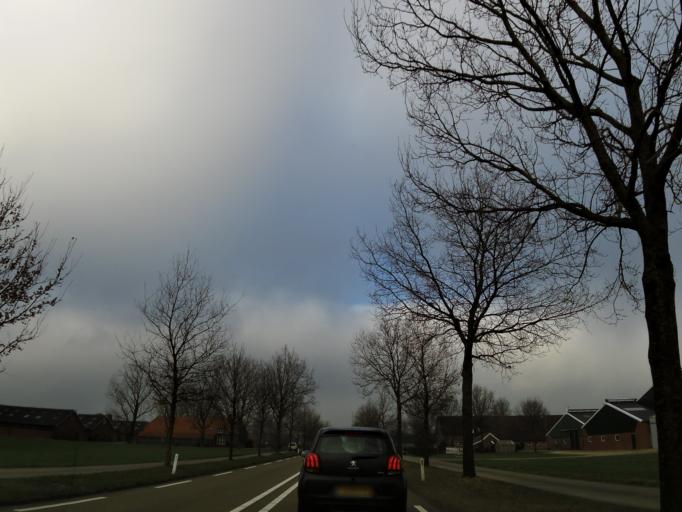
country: NL
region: North Brabant
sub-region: Gemeente Sint Anthonis
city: Sint Anthonis
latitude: 51.5450
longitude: 5.8214
